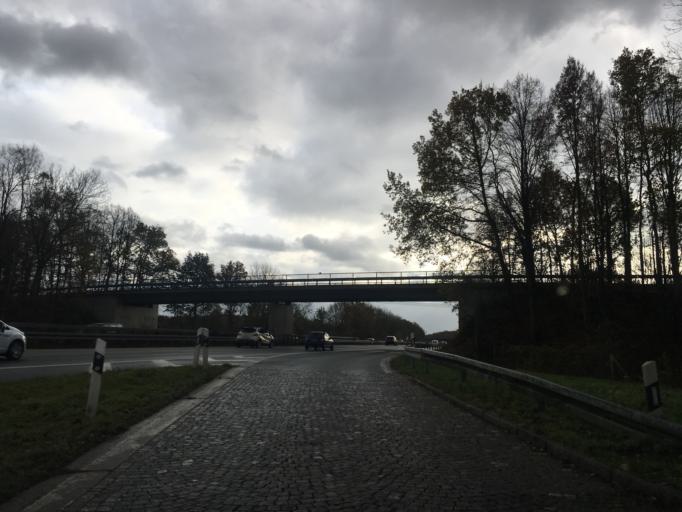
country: DE
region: North Rhine-Westphalia
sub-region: Regierungsbezirk Munster
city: Ascheberg
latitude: 51.8391
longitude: 7.5879
